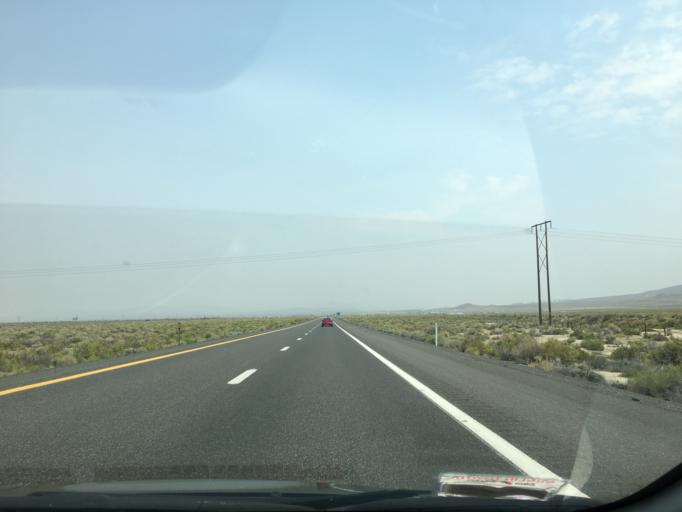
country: US
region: Nevada
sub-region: Lyon County
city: Fernley
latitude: 39.7755
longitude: -119.0318
